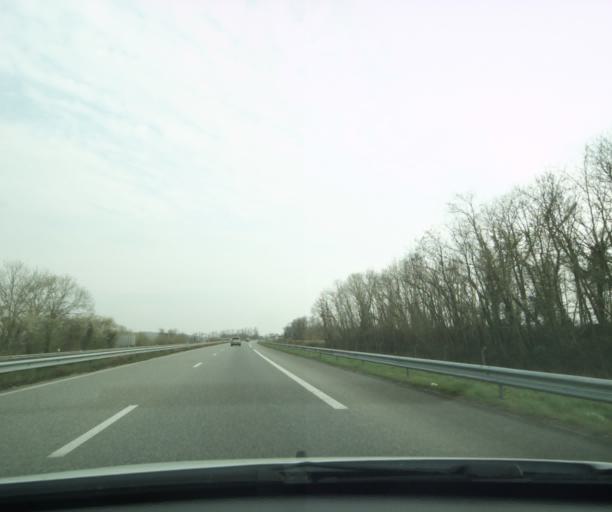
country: FR
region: Aquitaine
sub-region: Departement des Pyrenees-Atlantiques
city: Artix
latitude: 43.4105
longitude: -0.5649
